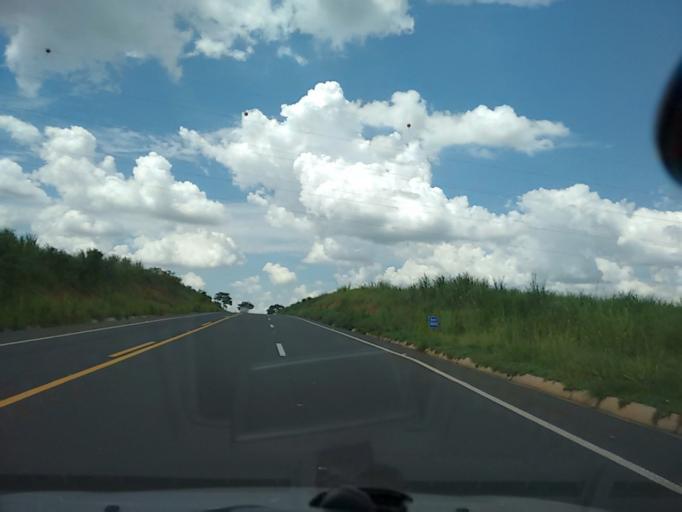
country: BR
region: Sao Paulo
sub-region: Osvaldo Cruz
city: Osvaldo Cruz
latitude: -21.8686
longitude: -50.8532
